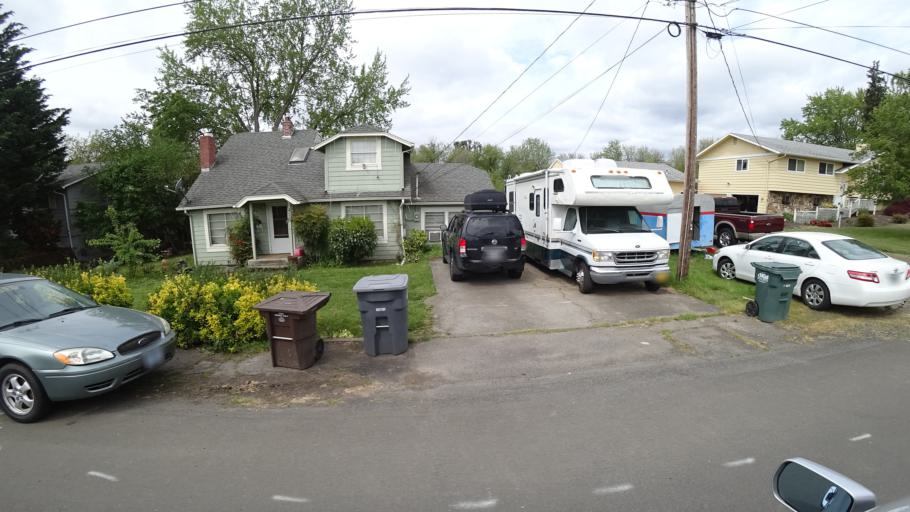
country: US
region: Oregon
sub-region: Washington County
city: Hillsboro
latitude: 45.5272
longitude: -123.0034
